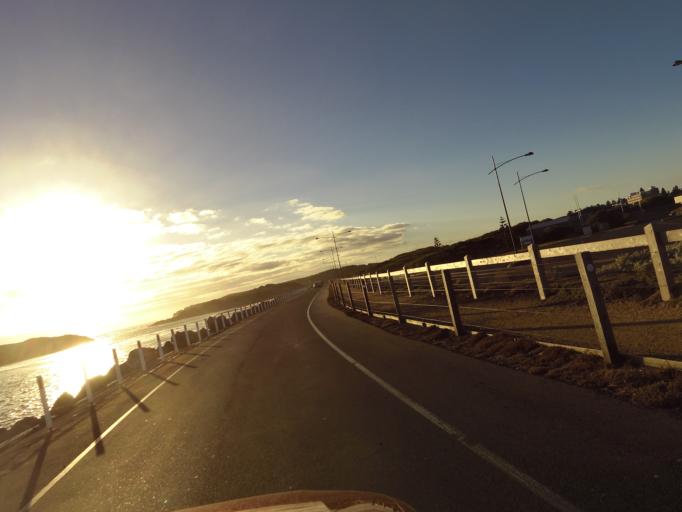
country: AU
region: Victoria
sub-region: Warrnambool
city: Warrnambool
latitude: -38.4025
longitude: 142.4752
